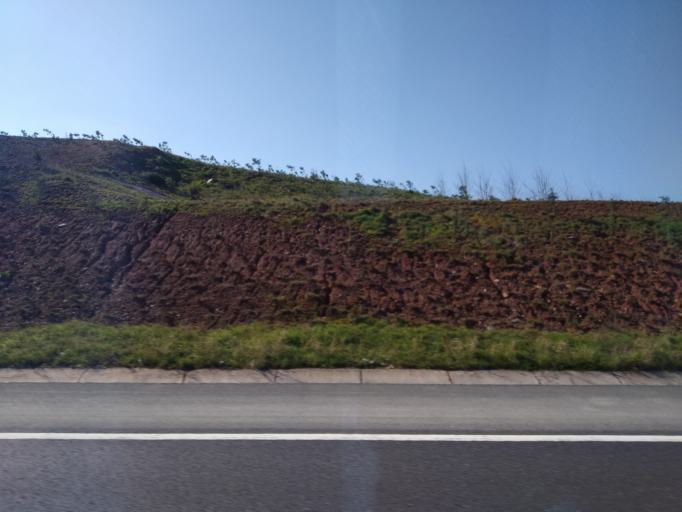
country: TR
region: Istanbul
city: Mahmut Sevket Pasa
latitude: 41.1199
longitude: 29.2875
